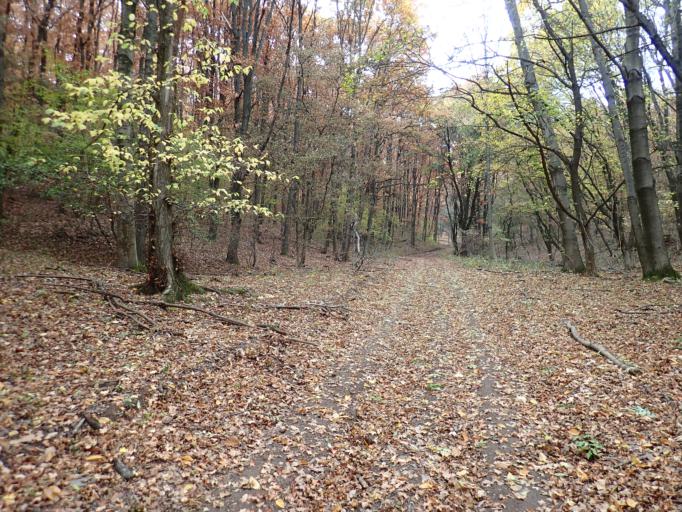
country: HU
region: Borsod-Abauj-Zemplen
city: Bogacs
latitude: 47.9656
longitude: 20.5178
